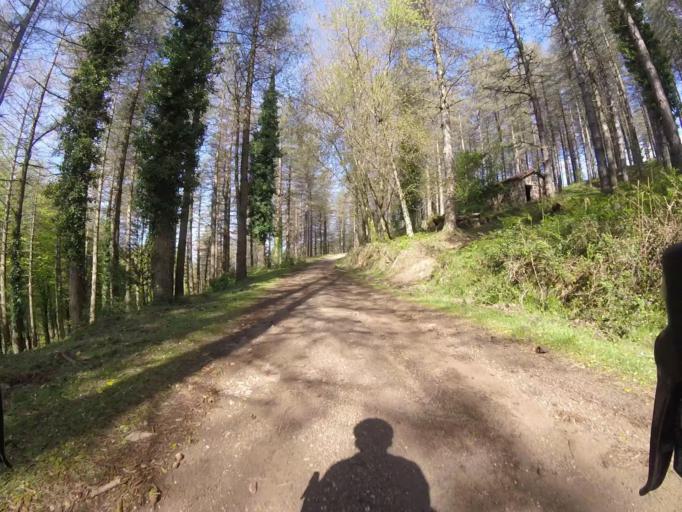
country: ES
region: Basque Country
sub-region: Provincia de Guipuzcoa
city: Andoain
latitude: 43.1960
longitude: -1.9784
